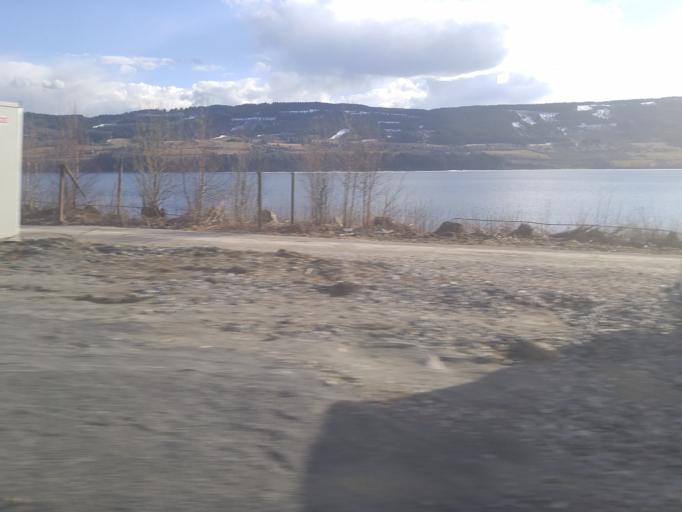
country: NO
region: Oppland
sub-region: Lillehammer
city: Lillehammer
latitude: 61.0081
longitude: 10.5586
